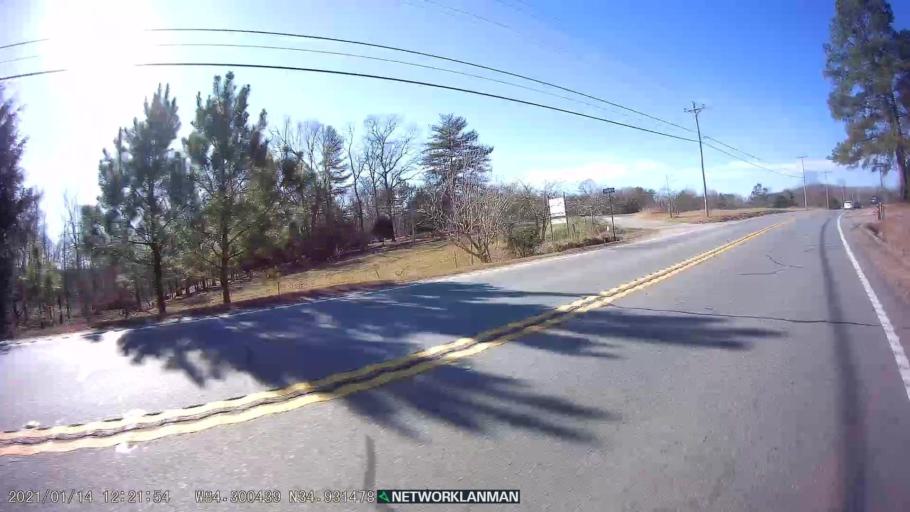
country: US
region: Georgia
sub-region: Fannin County
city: Blue Ridge
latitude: 34.9317
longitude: -84.3007
